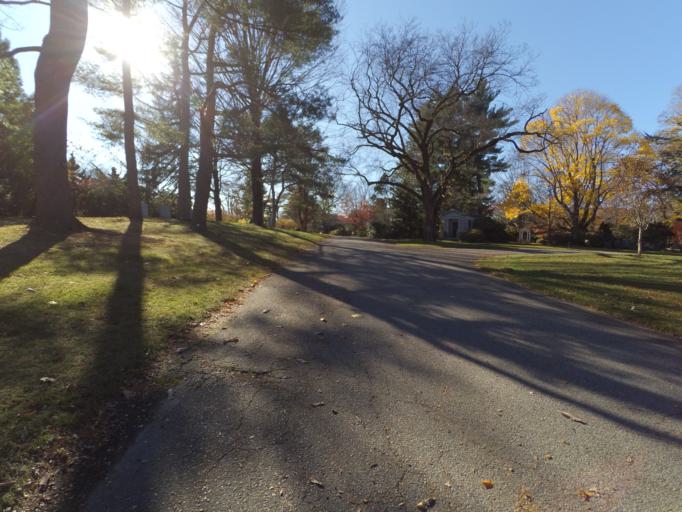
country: US
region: Massachusetts
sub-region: Middlesex County
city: Cambridge
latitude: 42.3671
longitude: -71.1425
